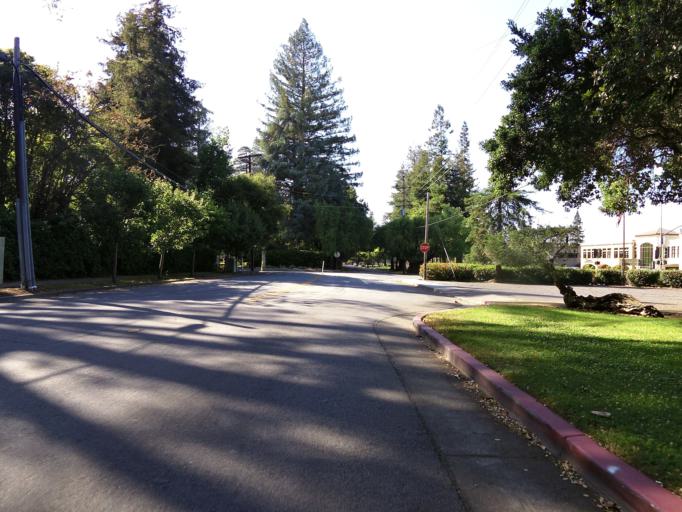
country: US
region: California
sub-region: Santa Clara County
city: Los Altos
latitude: 37.3768
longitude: -122.1185
